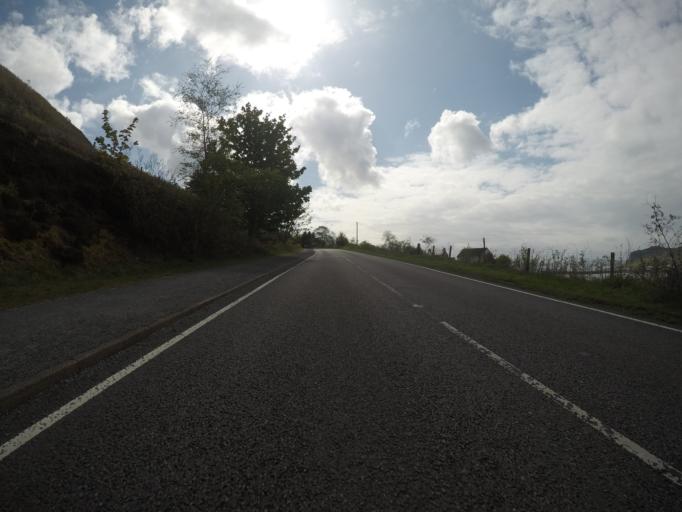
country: GB
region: Scotland
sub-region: Highland
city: Portree
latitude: 57.5880
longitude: -6.3557
